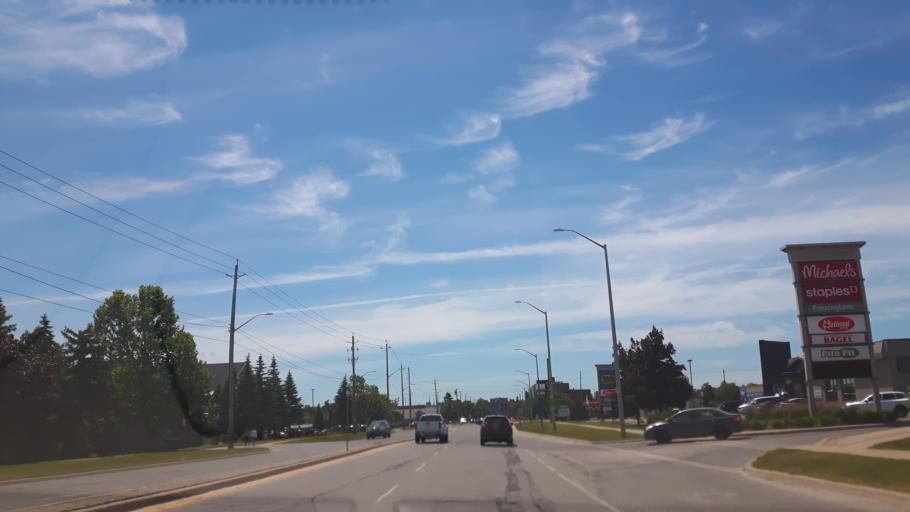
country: CA
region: Ontario
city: London
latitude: 43.0288
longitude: -81.2839
